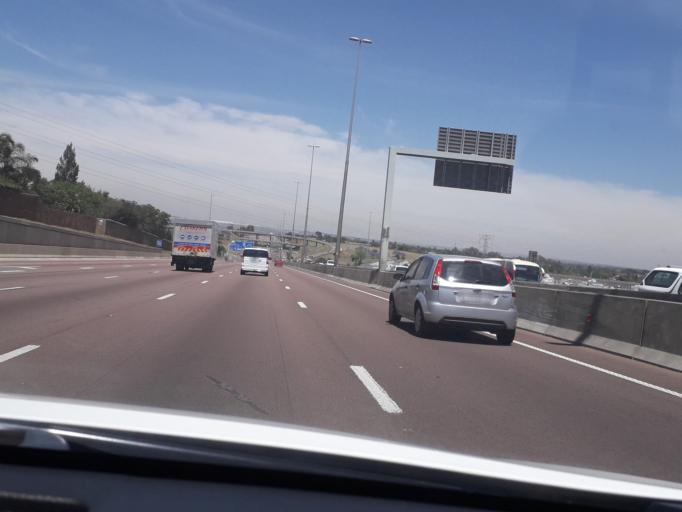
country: ZA
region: Gauteng
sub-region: City of Tshwane Metropolitan Municipality
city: Centurion
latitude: -25.8219
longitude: 28.2510
